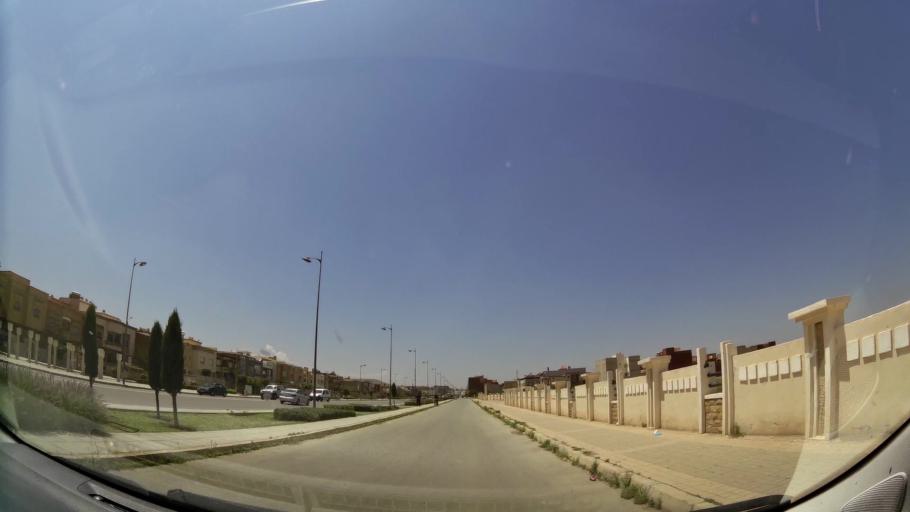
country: MA
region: Oriental
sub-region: Oujda-Angad
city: Oujda
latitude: 34.6667
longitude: -1.9417
